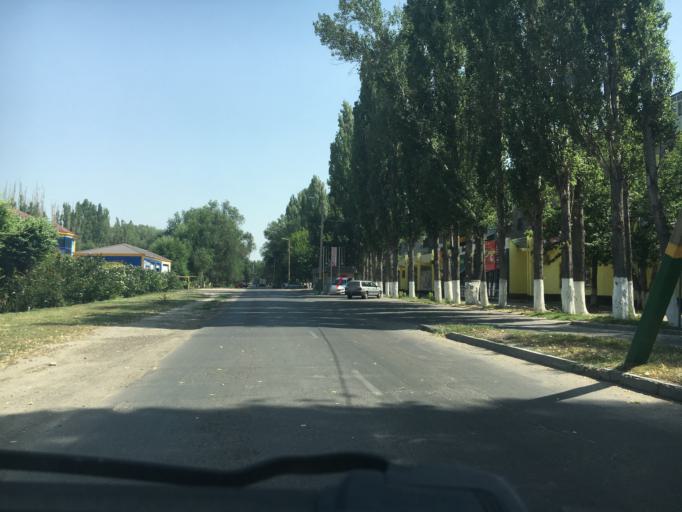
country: KZ
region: Zhambyl
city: Taraz
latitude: 42.8879
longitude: 71.3445
